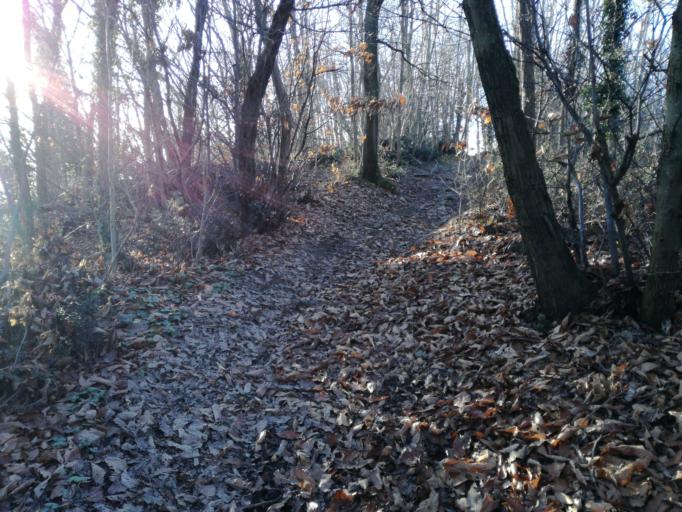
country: IT
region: Veneto
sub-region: Provincia di Padova
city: Galzignano
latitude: 45.3031
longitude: 11.7307
